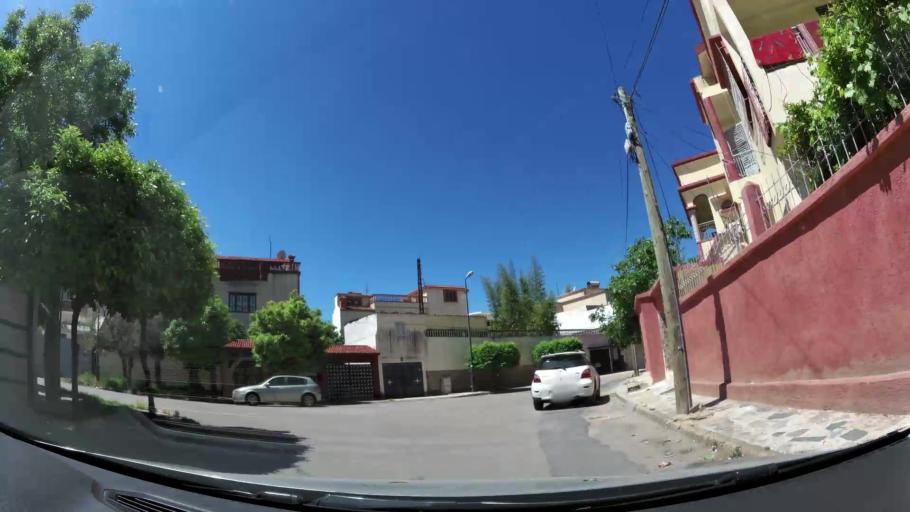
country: MA
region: Meknes-Tafilalet
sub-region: Meknes
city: Meknes
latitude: 33.8895
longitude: -5.5464
